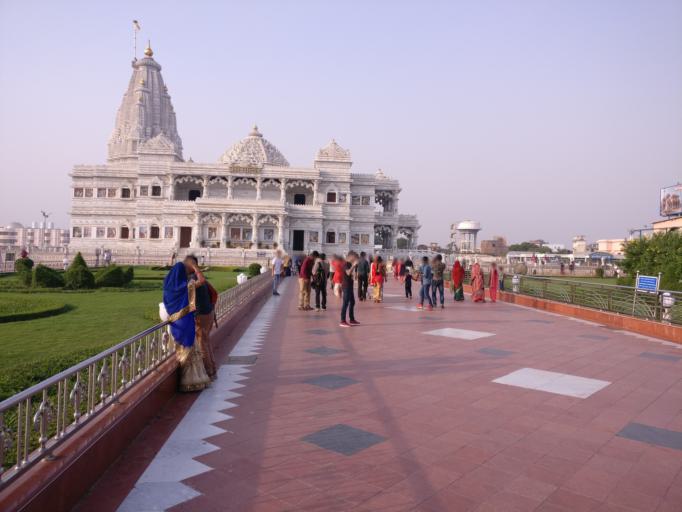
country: IN
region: Uttar Pradesh
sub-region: Mathura
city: Vrindavan
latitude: 27.5713
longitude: 77.6720
